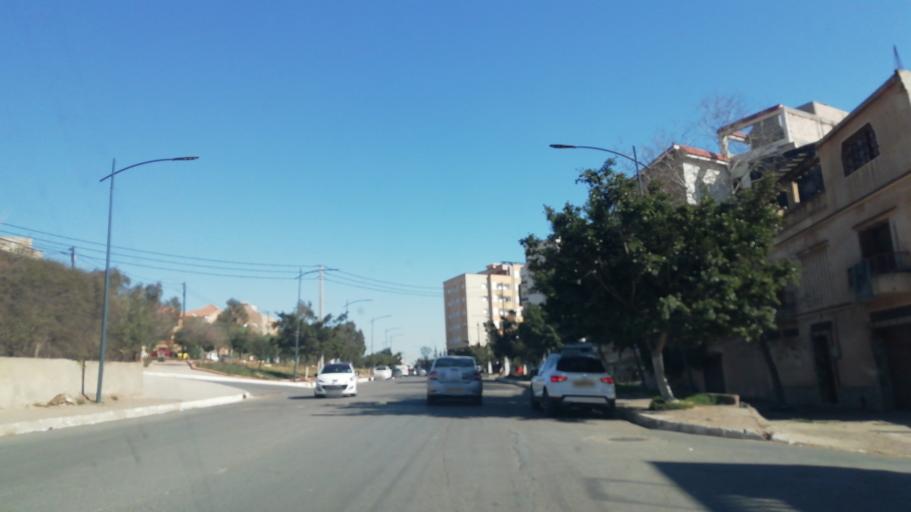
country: DZ
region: Oran
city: Bir el Djir
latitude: 35.7161
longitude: -0.5832
